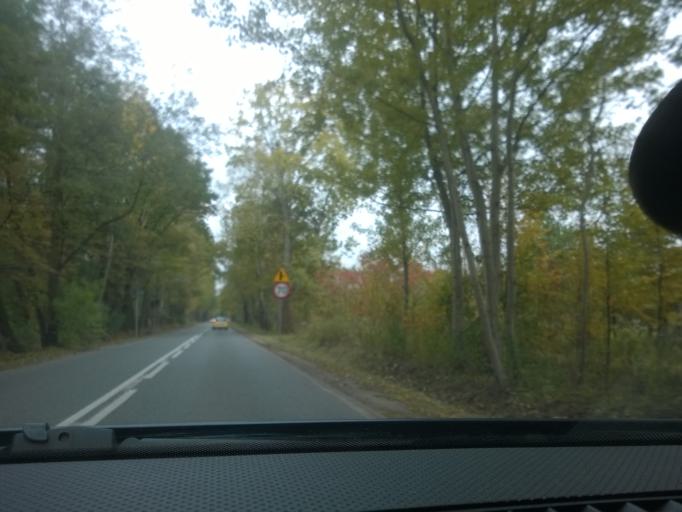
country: PL
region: Masovian Voivodeship
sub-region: Powiat pruszkowski
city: Granica
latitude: 52.1281
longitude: 20.7995
